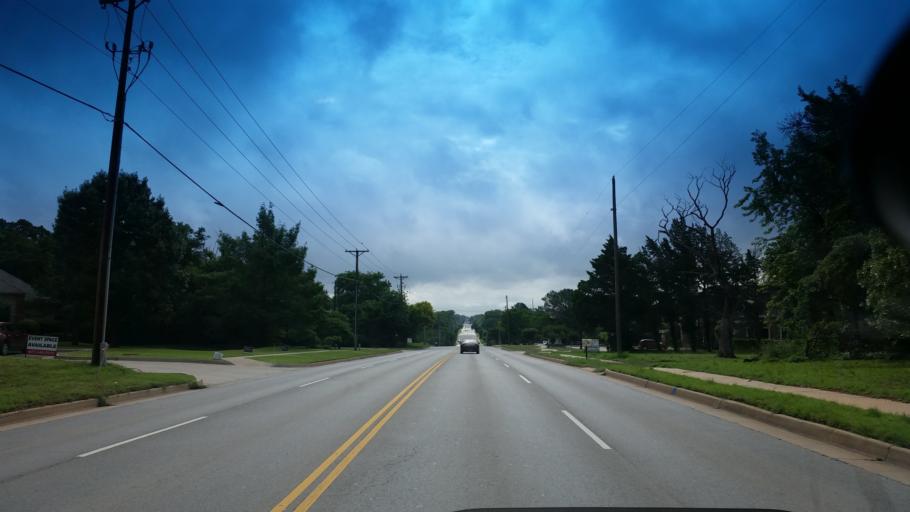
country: US
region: Oklahoma
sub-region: Oklahoma County
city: Edmond
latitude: 35.6383
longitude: -97.4576
